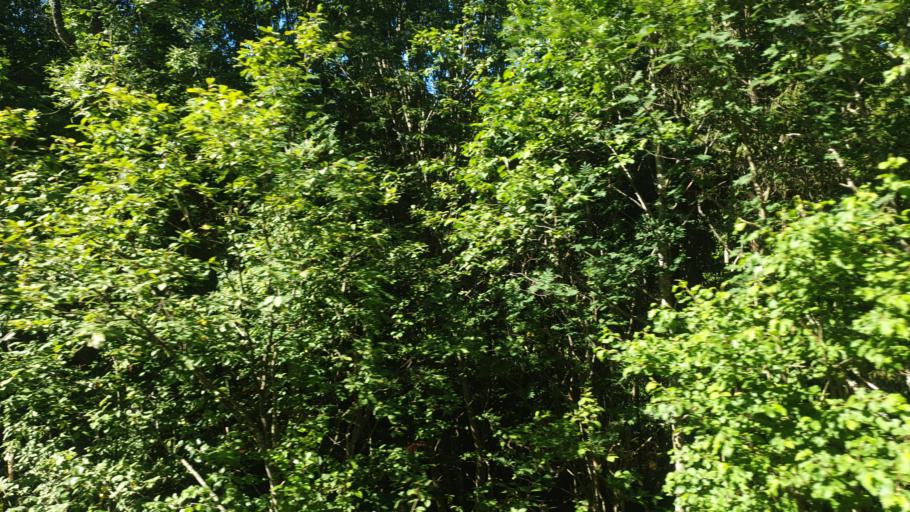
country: NO
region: Sor-Trondelag
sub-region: Meldal
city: Meldal
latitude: 63.1450
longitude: 9.7147
